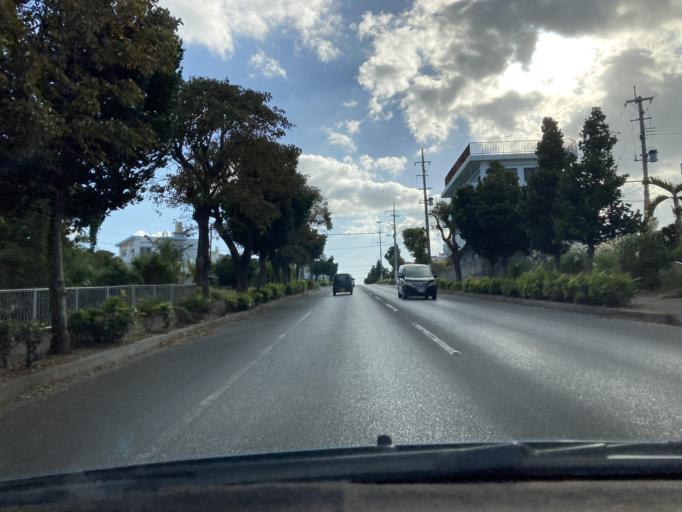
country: JP
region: Okinawa
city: Gushikawa
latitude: 26.3624
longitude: 127.8524
